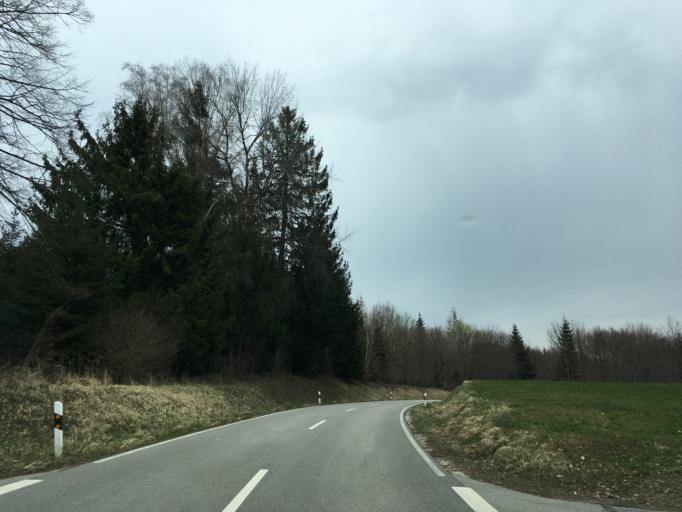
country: DE
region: Bavaria
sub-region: Upper Bavaria
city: Jettenbach
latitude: 48.1160
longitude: 12.3958
